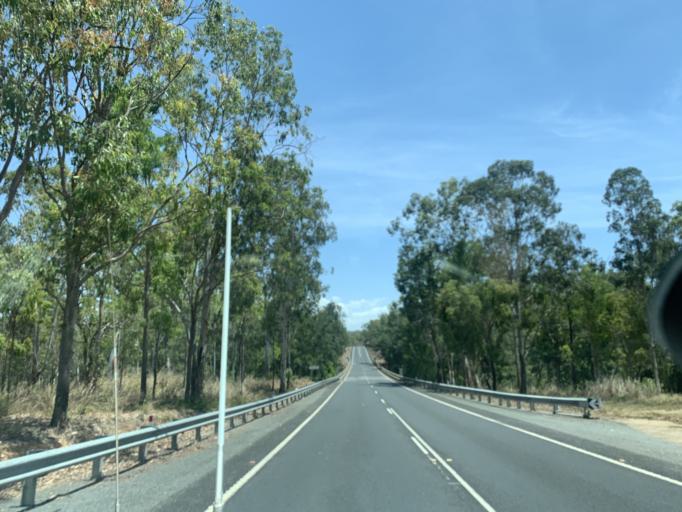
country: AU
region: Queensland
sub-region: Tablelands
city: Mareeba
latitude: -16.9415
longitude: 145.5418
